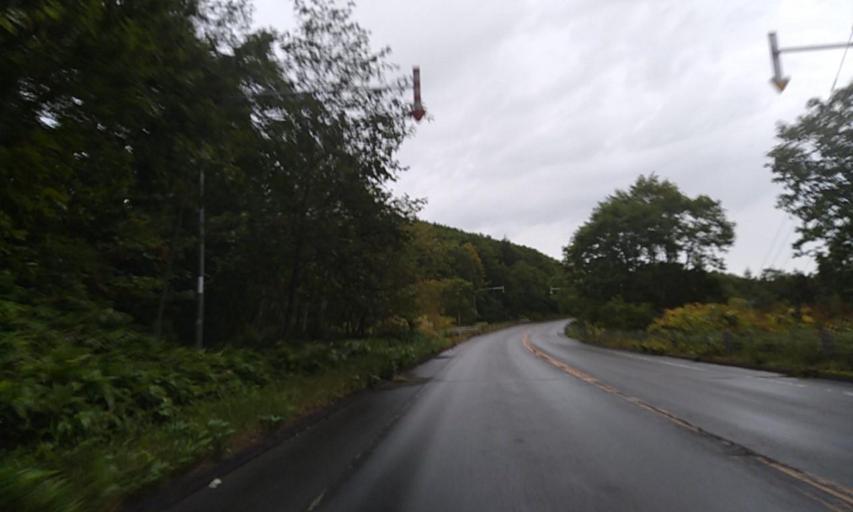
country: JP
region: Hokkaido
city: Mombetsu
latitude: 44.4880
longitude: 143.0842
